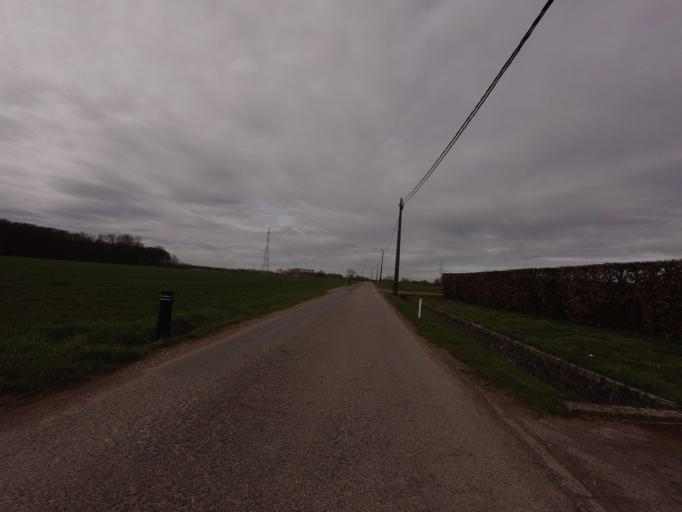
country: BE
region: Flanders
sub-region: Provincie Antwerpen
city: Lint
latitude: 51.1387
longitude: 4.5266
